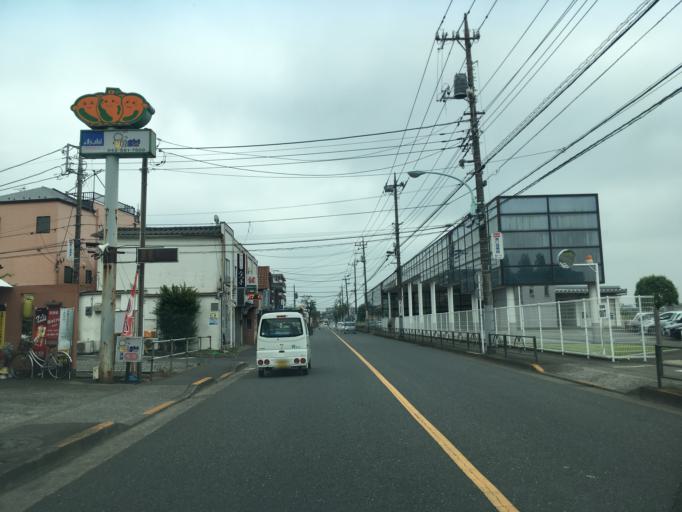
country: JP
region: Tokyo
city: Hino
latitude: 35.7398
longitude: 139.3941
